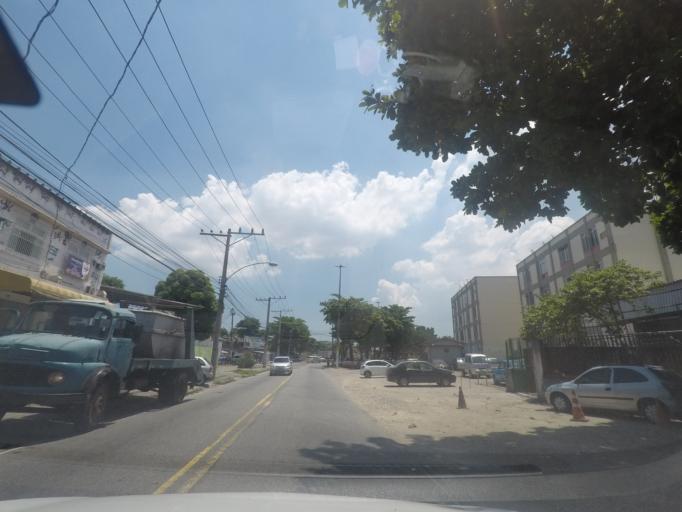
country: BR
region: Rio de Janeiro
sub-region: Duque De Caxias
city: Duque de Caxias
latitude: -22.8226
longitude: -43.3078
